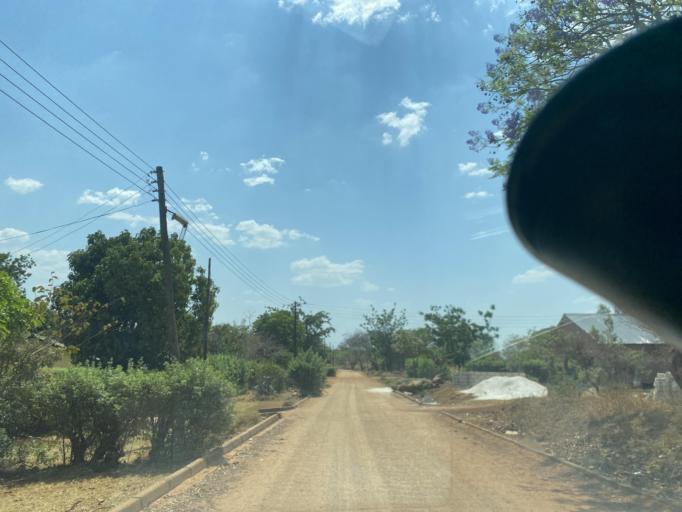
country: ZM
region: Lusaka
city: Kafue
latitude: -15.5059
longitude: 27.9356
